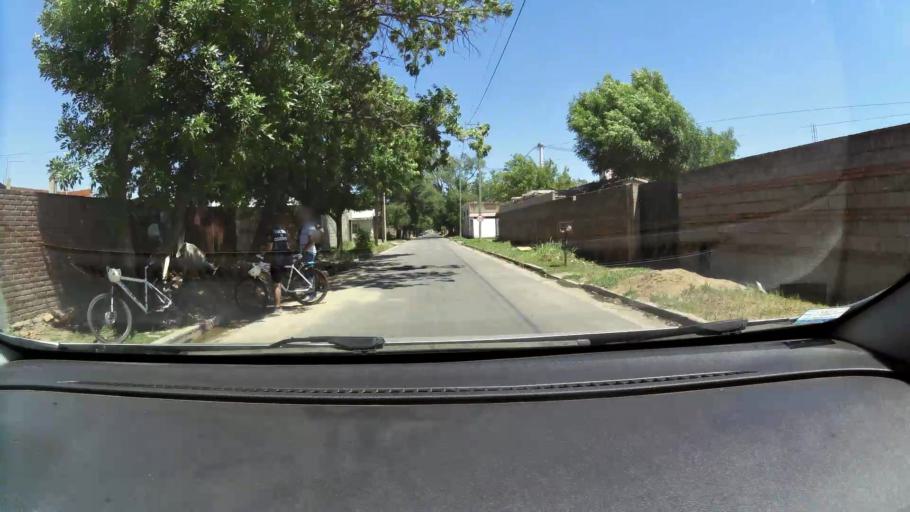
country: AR
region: Cordoba
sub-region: Departamento de Capital
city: Cordoba
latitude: -31.4364
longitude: -64.1199
